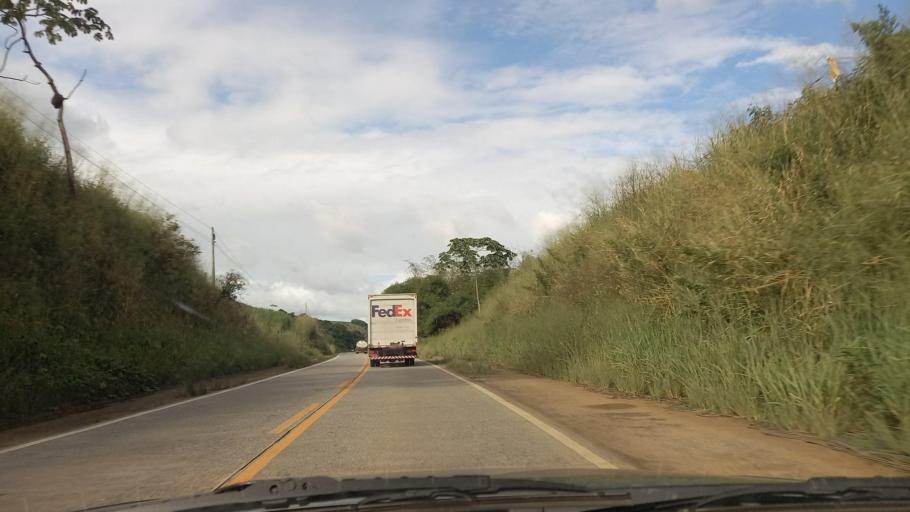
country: BR
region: Pernambuco
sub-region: Palmares
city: Palmares
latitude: -8.6938
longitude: -35.6438
